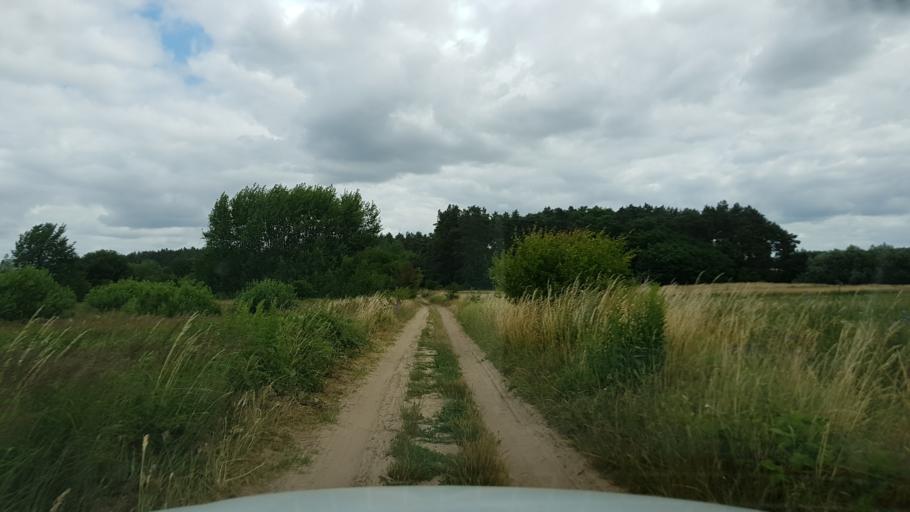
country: PL
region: West Pomeranian Voivodeship
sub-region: Powiat mysliborski
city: Mysliborz
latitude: 52.9352
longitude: 14.8896
